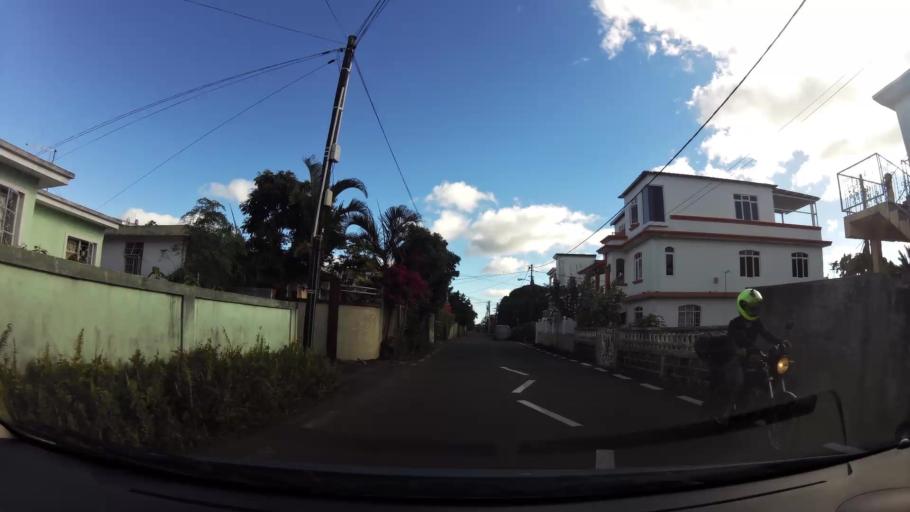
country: MU
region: Plaines Wilhems
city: Vacoas
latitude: -20.2963
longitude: 57.4888
